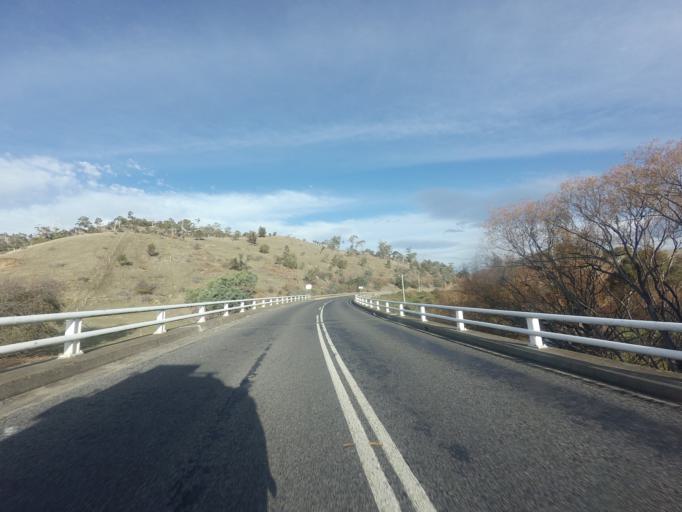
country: AU
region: Tasmania
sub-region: Brighton
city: Bridgewater
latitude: -42.4385
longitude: 147.1507
